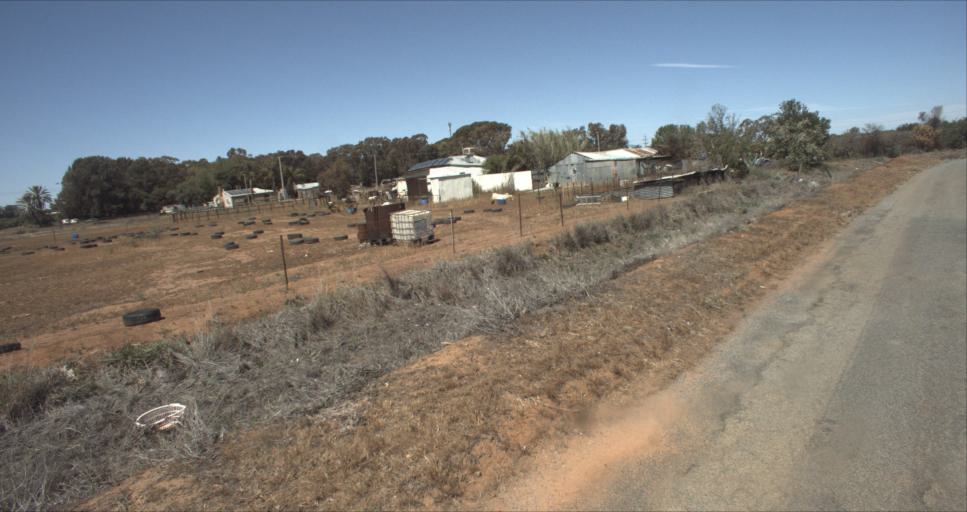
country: AU
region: New South Wales
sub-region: Leeton
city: Leeton
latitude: -34.5293
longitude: 146.3321
